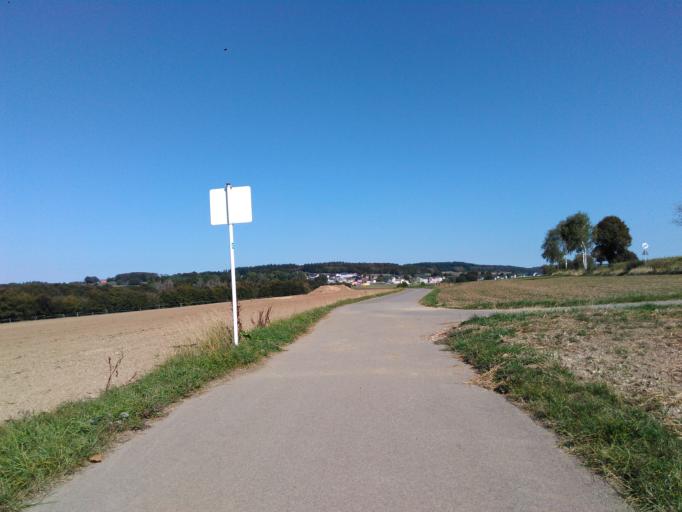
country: LU
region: Diekirch
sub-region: Canton de Redange
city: Rambrouch
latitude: 49.8190
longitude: 5.8373
